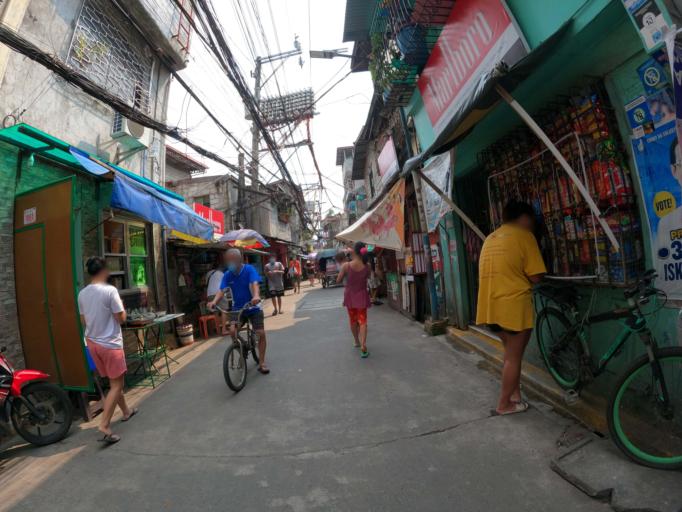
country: PH
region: Metro Manila
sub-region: San Juan
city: San Juan
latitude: 14.5840
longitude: 121.0111
